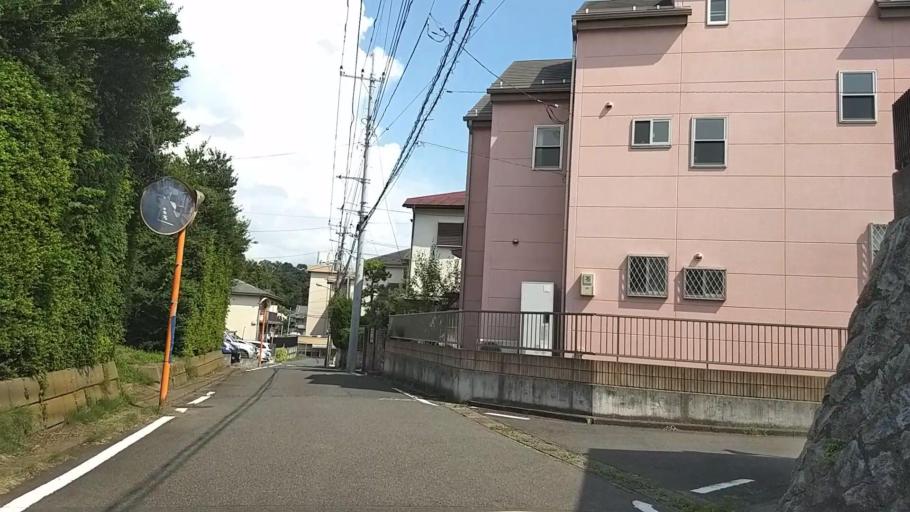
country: JP
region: Tokyo
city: Hachioji
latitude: 35.6474
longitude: 139.3119
